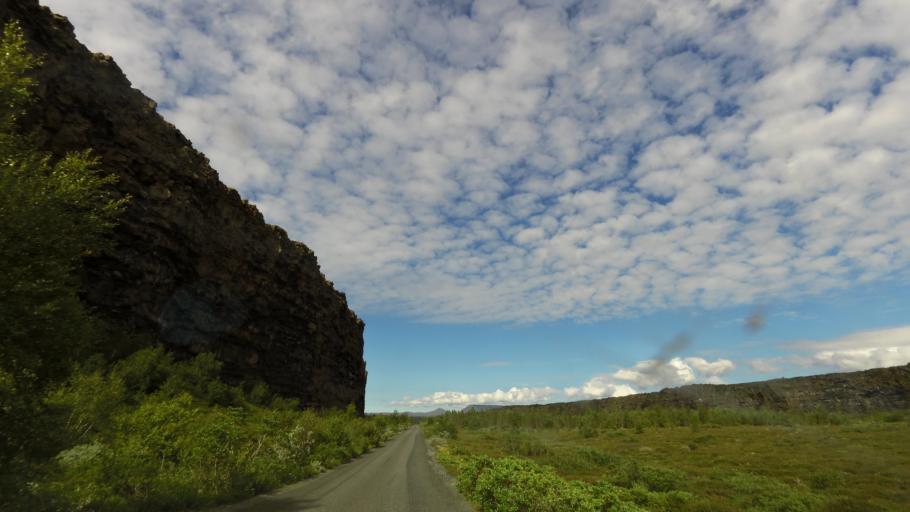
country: IS
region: Northeast
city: Husavik
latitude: 66.0124
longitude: -16.5032
